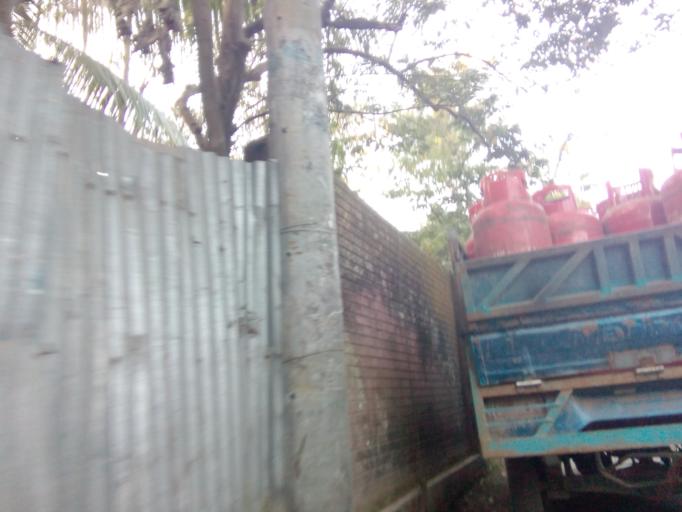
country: BD
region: Chittagong
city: Comilla
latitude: 23.4029
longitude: 91.1818
